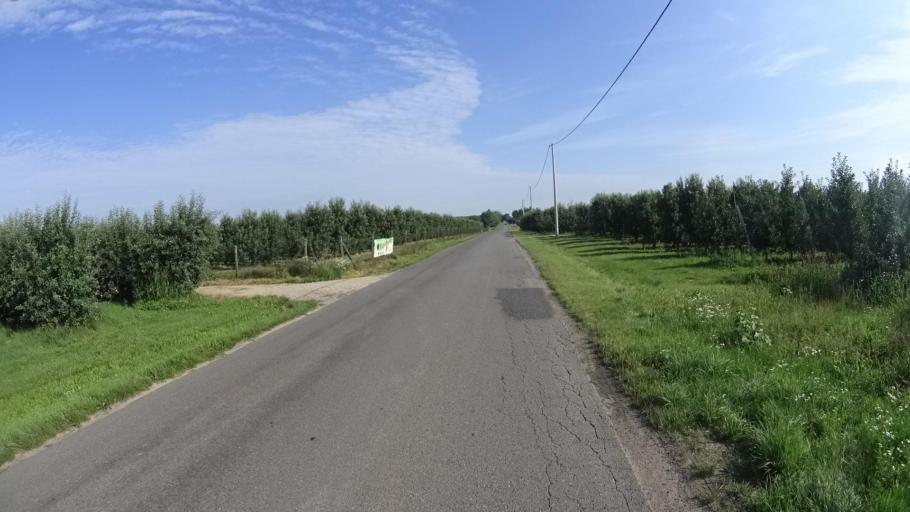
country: PL
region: Masovian Voivodeship
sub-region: Powiat grojecki
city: Goszczyn
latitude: 51.7592
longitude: 20.8531
